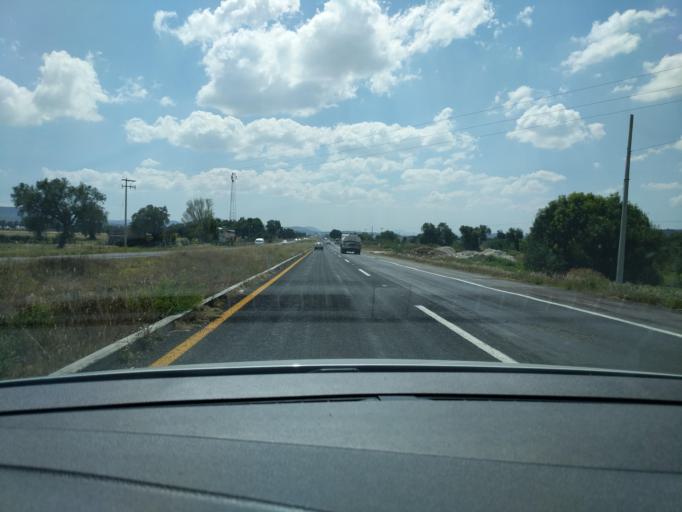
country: MX
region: Hidalgo
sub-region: Mineral de la Reforma
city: Rinconada de los Angeles
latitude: 19.9848
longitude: -98.7039
